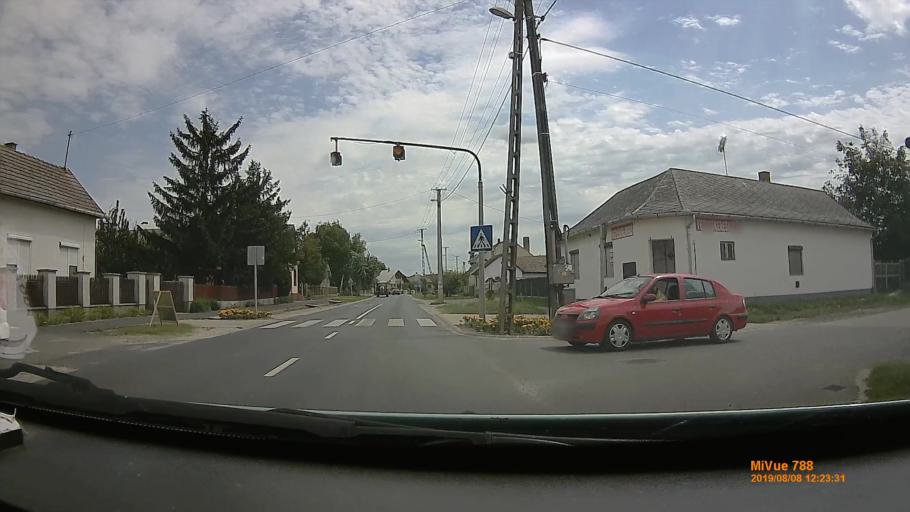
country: HU
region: Szabolcs-Szatmar-Bereg
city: Nyirbogat
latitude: 47.8021
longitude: 22.0590
